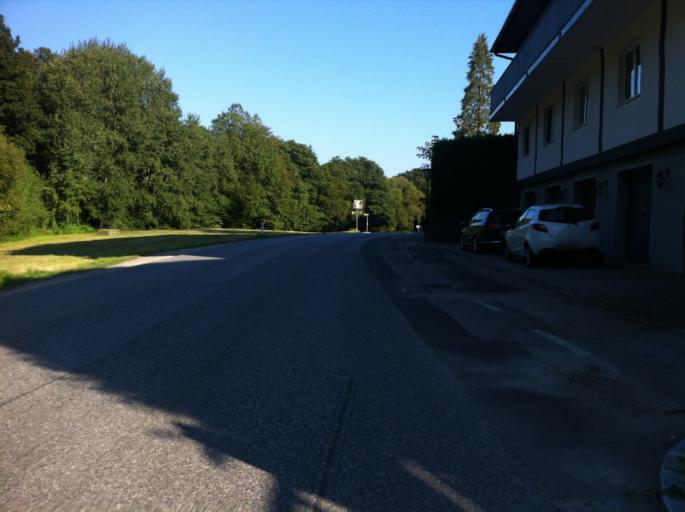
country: AT
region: Lower Austria
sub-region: Politischer Bezirk Wien-Umgebung
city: Pressbaum
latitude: 48.2023
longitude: 16.1076
